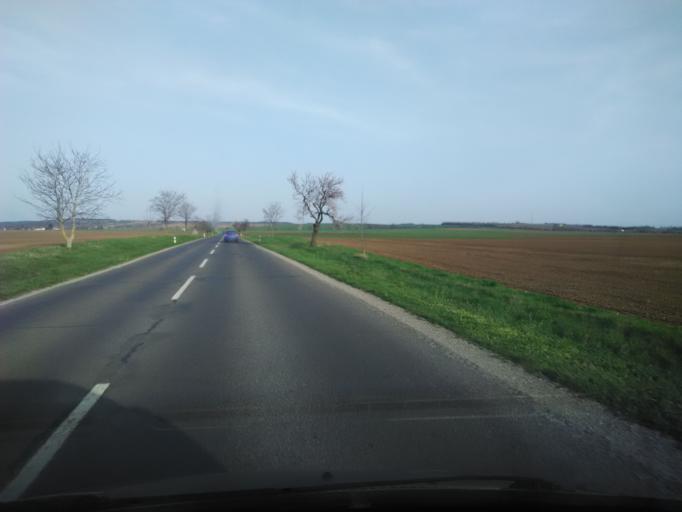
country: SK
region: Nitriansky
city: Surany
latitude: 48.0907
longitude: 18.2669
